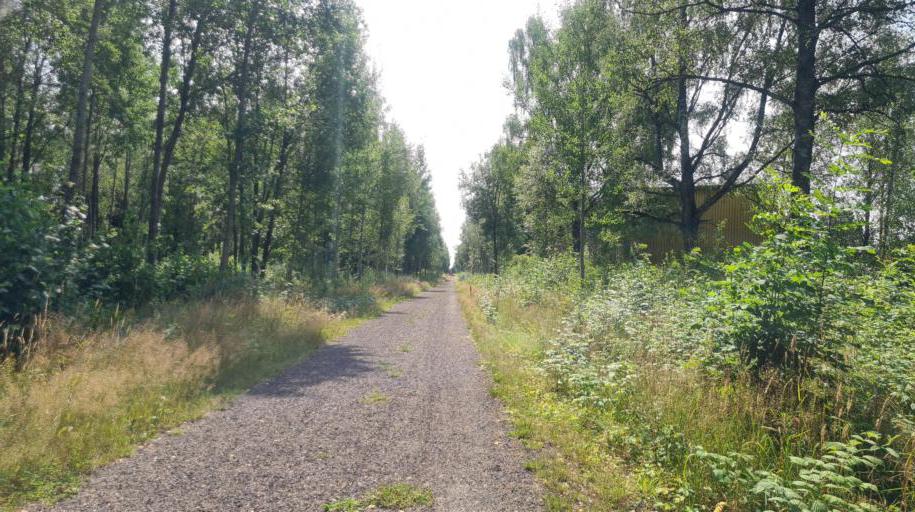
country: SE
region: Kronoberg
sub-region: Ljungby Kommun
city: Lagan
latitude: 56.9694
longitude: 13.9512
